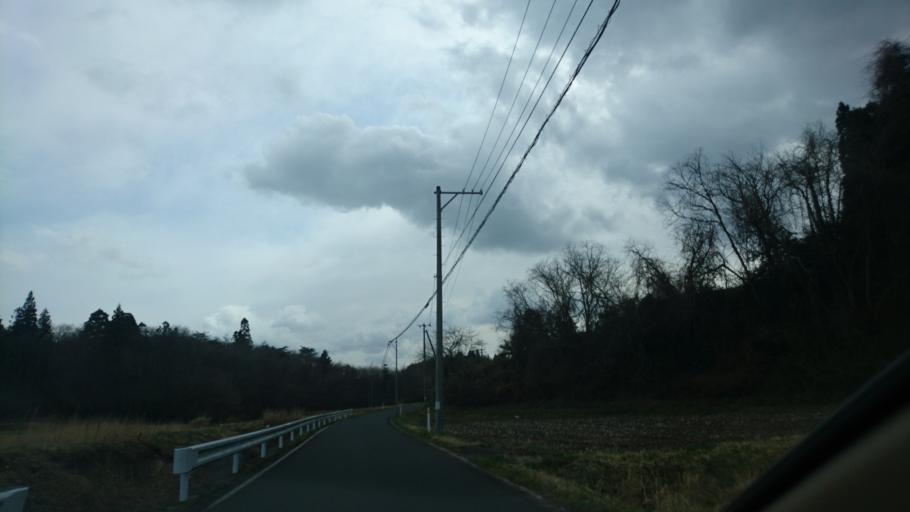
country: JP
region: Iwate
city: Ichinoseki
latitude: 38.8872
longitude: 141.1687
